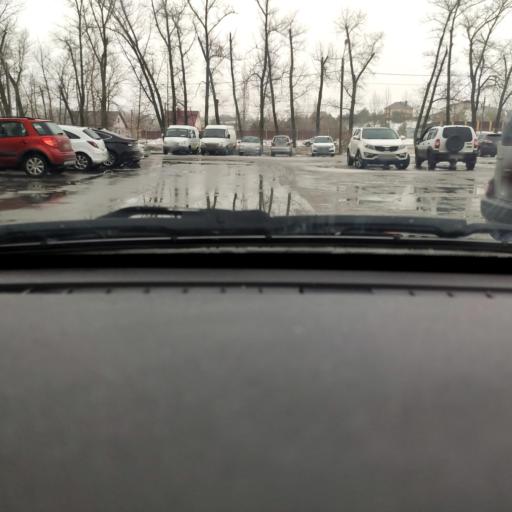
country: RU
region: Voronezj
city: Novaya Usman'
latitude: 51.6681
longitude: 39.4041
